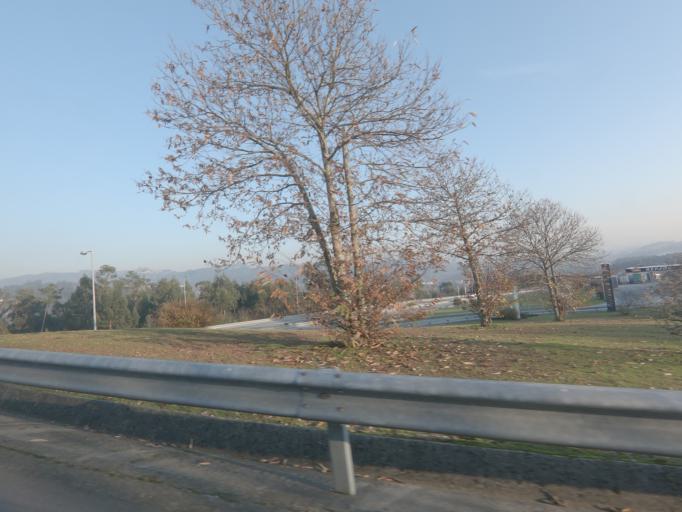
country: PT
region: Porto
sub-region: Marco de Canaveses
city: Marco de Canavezes
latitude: 41.2343
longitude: -8.1795
